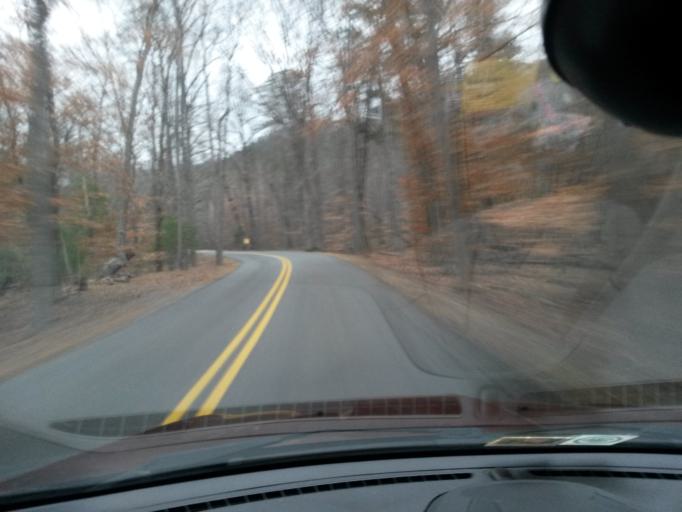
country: US
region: Virginia
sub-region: Alleghany County
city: Clifton Forge
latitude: 37.8849
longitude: -79.8052
